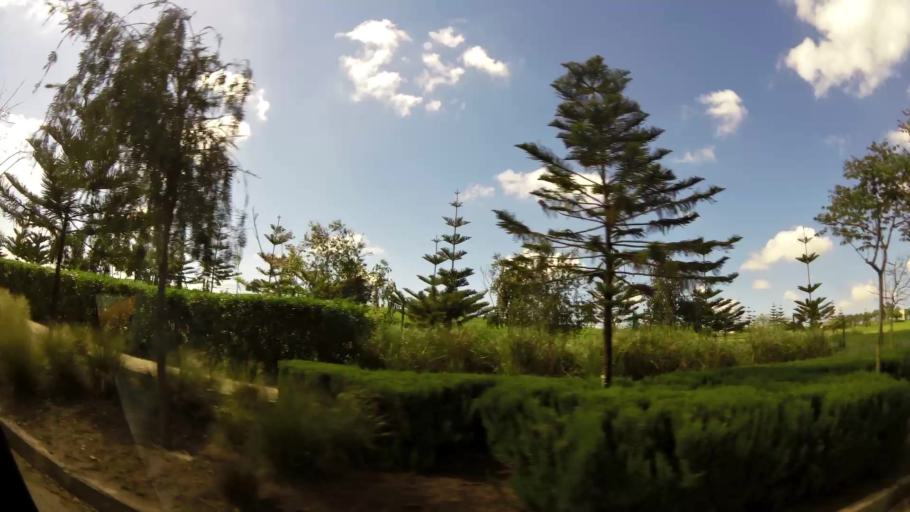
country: MA
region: Grand Casablanca
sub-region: Nouaceur
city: Bouskoura
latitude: 33.4766
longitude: -7.5942
